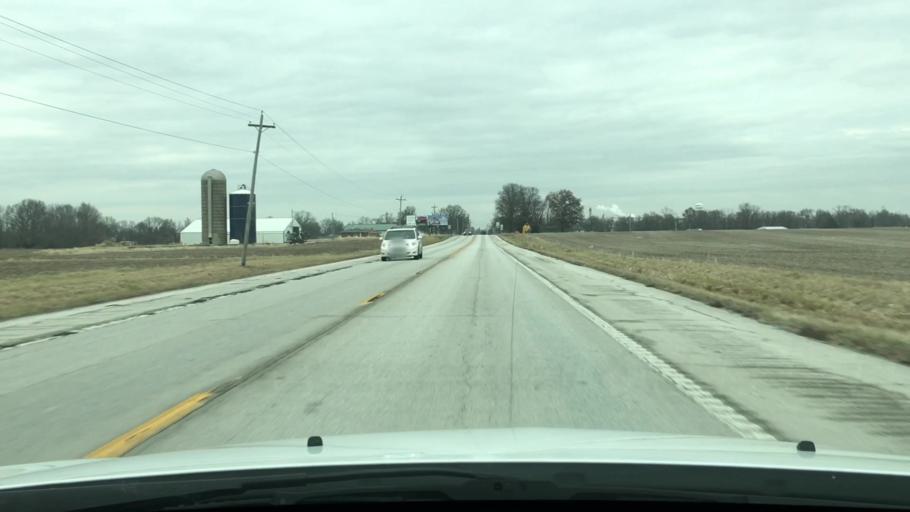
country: US
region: Missouri
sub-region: Audrain County
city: Vandalia
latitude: 39.2320
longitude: -91.6459
